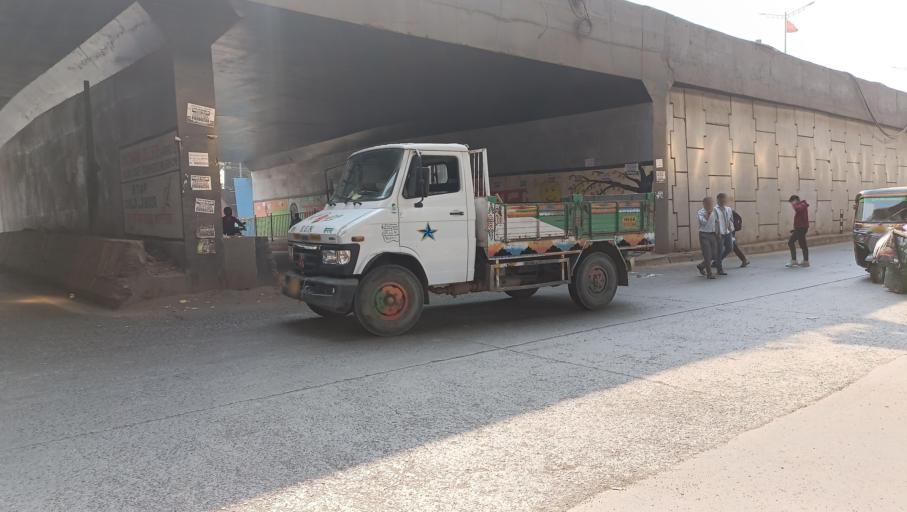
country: IN
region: Maharashtra
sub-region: Mumbai Suburban
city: Borivli
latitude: 19.2504
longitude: 72.8664
